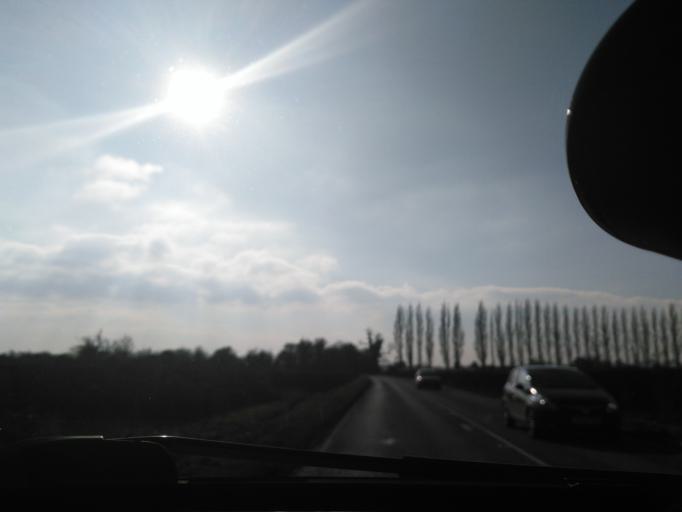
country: GB
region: England
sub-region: Wiltshire
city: Malmesbury
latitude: 51.5468
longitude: -2.1199
